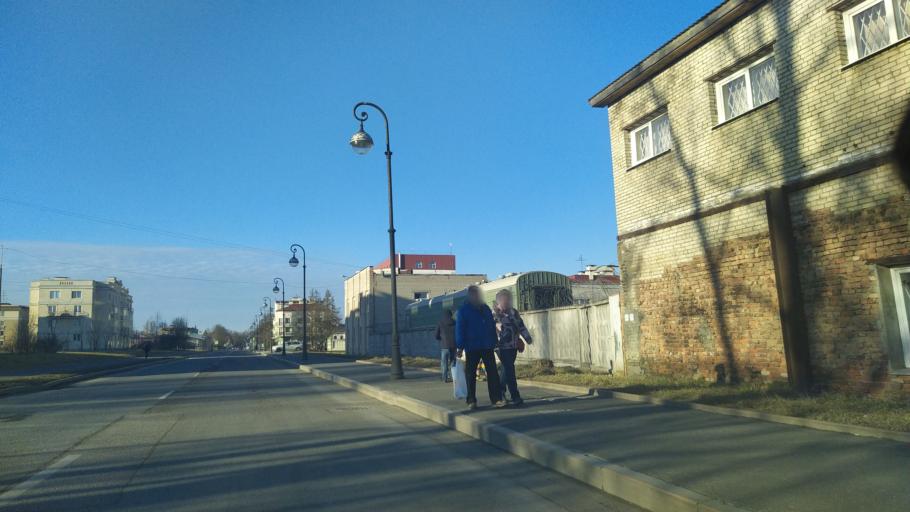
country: RU
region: St.-Petersburg
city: Pushkin
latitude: 59.7016
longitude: 30.3940
